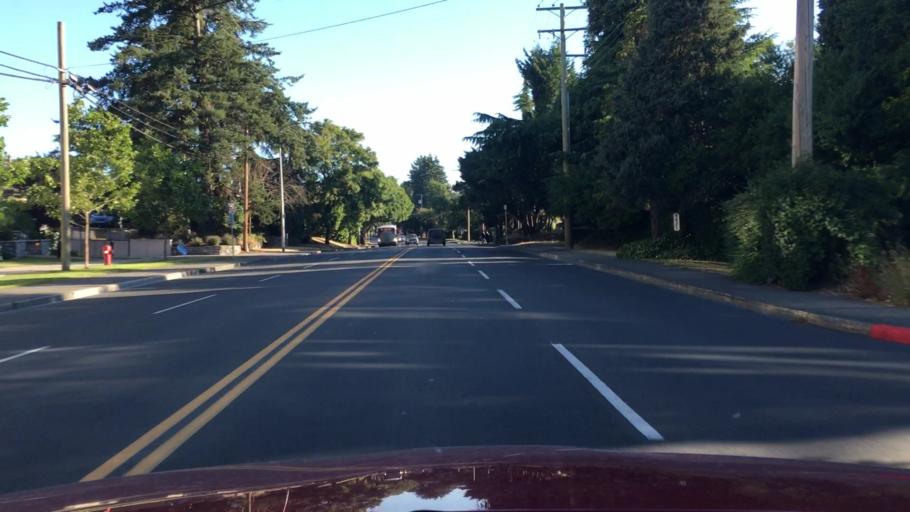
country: CA
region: British Columbia
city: Oak Bay
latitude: 48.4733
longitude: -123.3326
